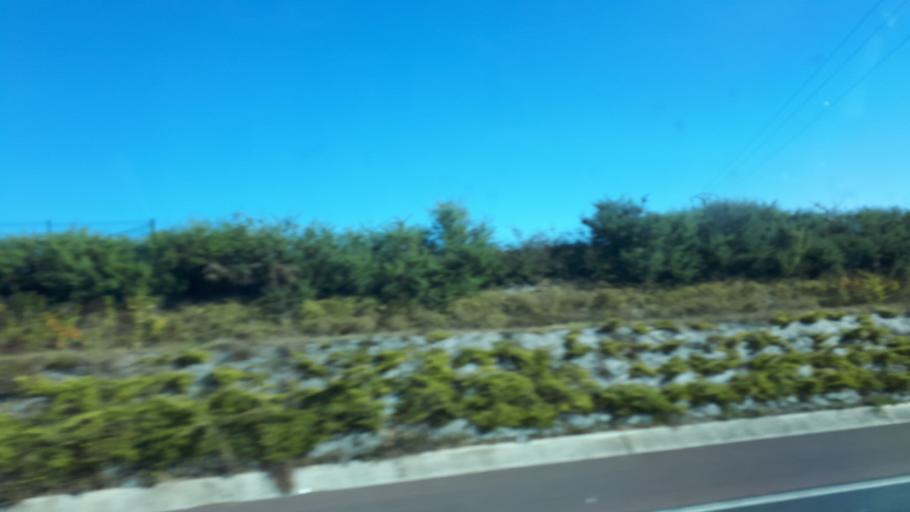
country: FR
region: Centre
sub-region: Departement d'Eure-et-Loir
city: Chateaudun
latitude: 48.0604
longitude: 1.3361
